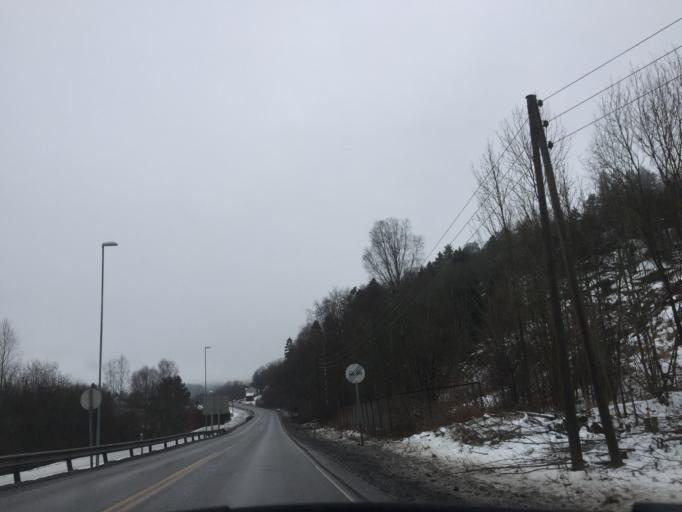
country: NO
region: Akershus
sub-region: Frogn
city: Drobak
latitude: 59.6841
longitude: 10.6677
